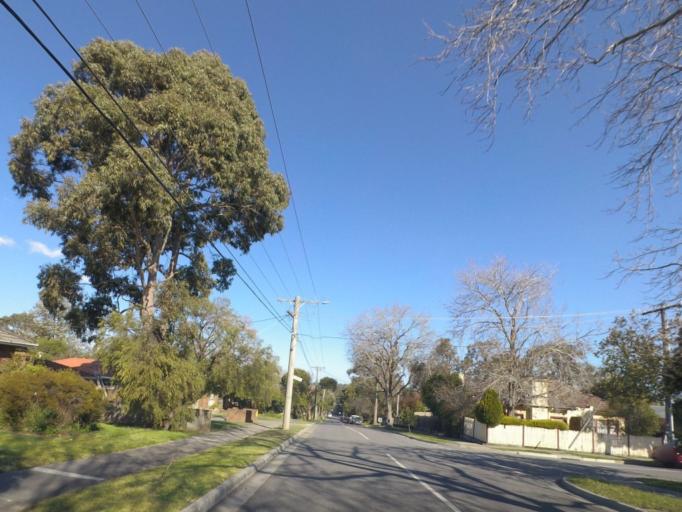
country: AU
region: Victoria
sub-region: Maroondah
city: Ringwood East
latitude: -37.8202
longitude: 145.2342
